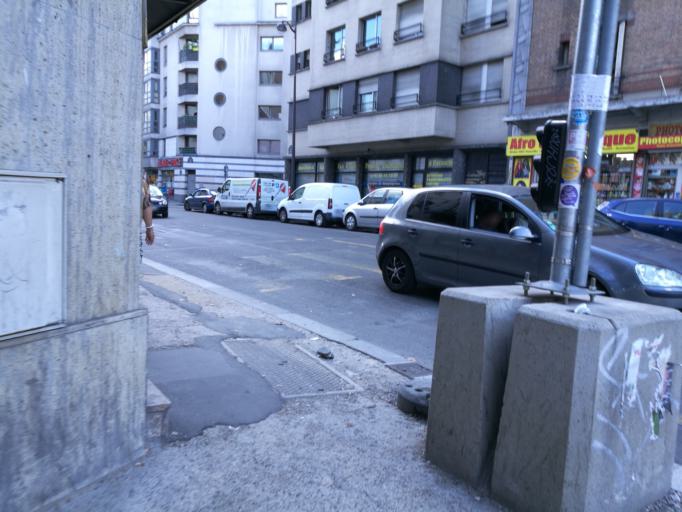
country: FR
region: Ile-de-France
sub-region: Paris
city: Saint-Ouen
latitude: 48.8976
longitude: 2.3376
